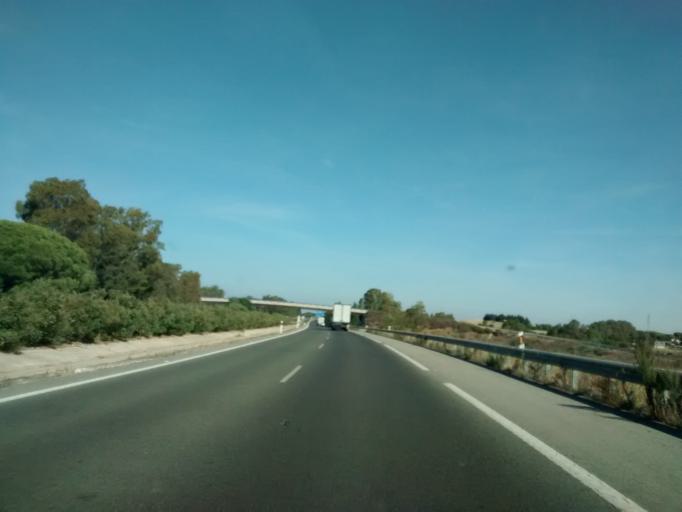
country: ES
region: Andalusia
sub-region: Provincia de Cadiz
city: Chiclana de la Frontera
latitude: 36.3884
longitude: -6.1180
